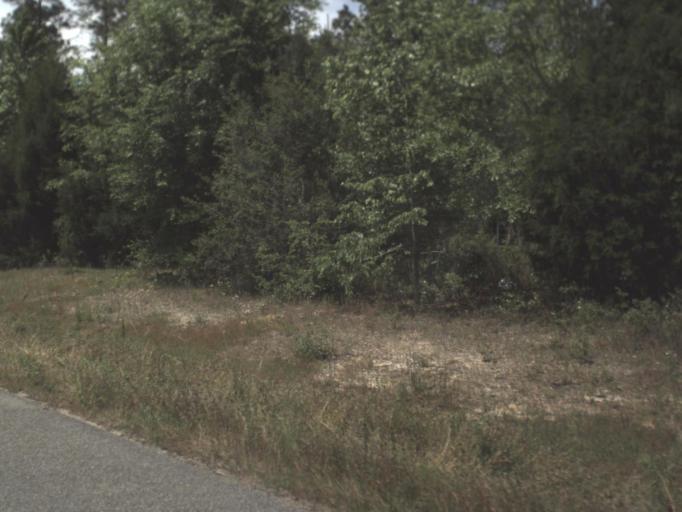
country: US
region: Florida
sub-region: Calhoun County
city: Blountstown
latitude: 30.5779
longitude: -85.1826
